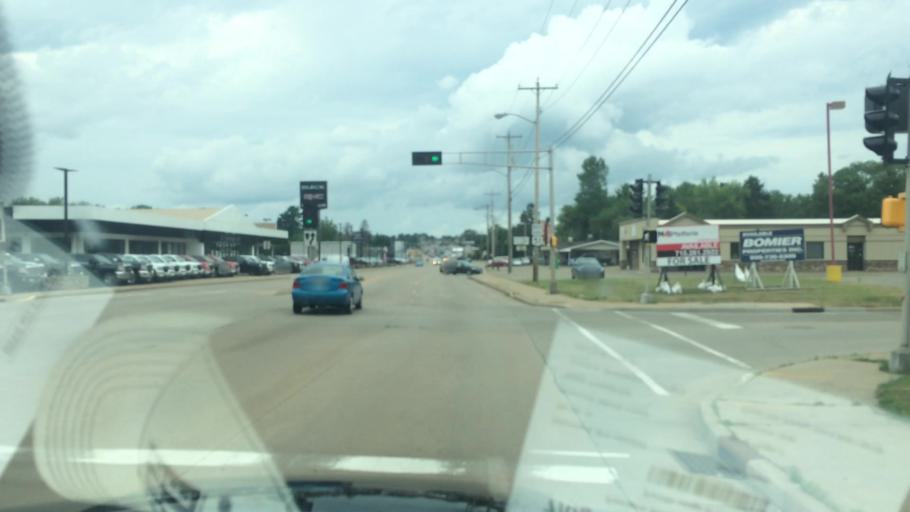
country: US
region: Wisconsin
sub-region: Marathon County
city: Schofield
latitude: 44.9253
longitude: -89.6134
